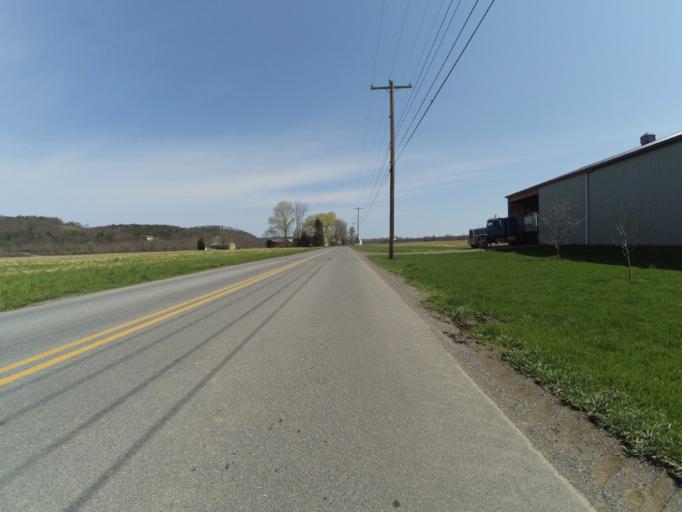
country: US
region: Pennsylvania
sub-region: Clinton County
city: Dunnstown
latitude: 41.1474
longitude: -77.3912
